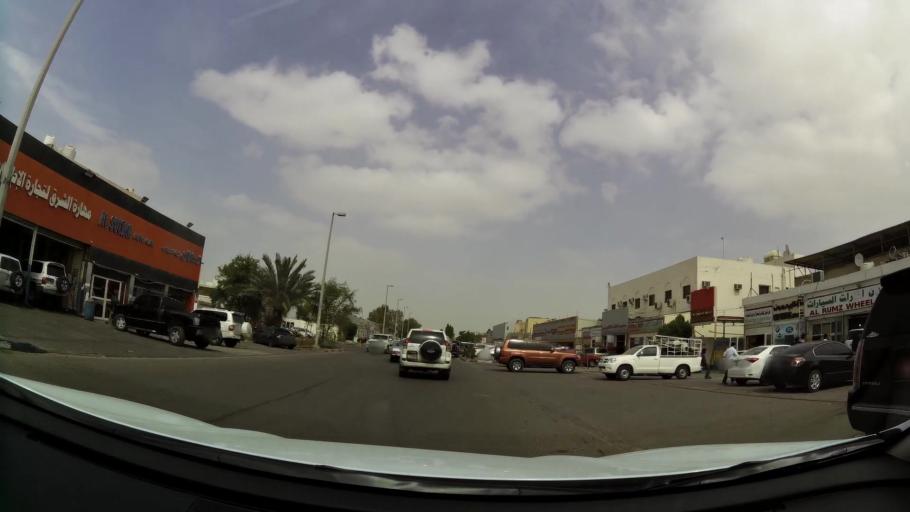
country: AE
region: Abu Dhabi
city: Abu Dhabi
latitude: 24.3787
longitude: 54.5147
